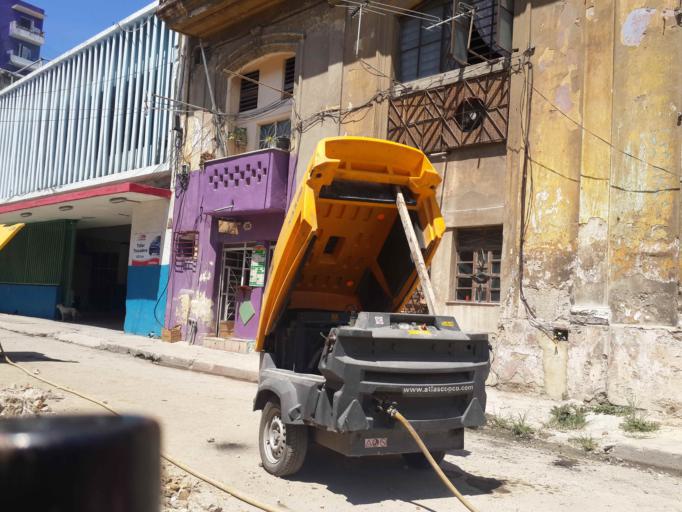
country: CU
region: La Habana
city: Centro Habana
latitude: 23.1411
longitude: -82.3630
